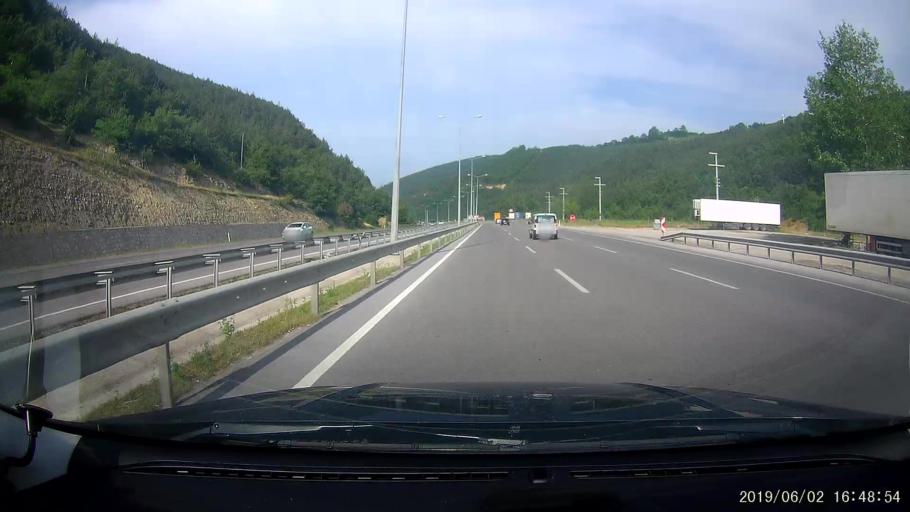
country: TR
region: Samsun
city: Taflan
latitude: 41.2316
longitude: 36.1490
